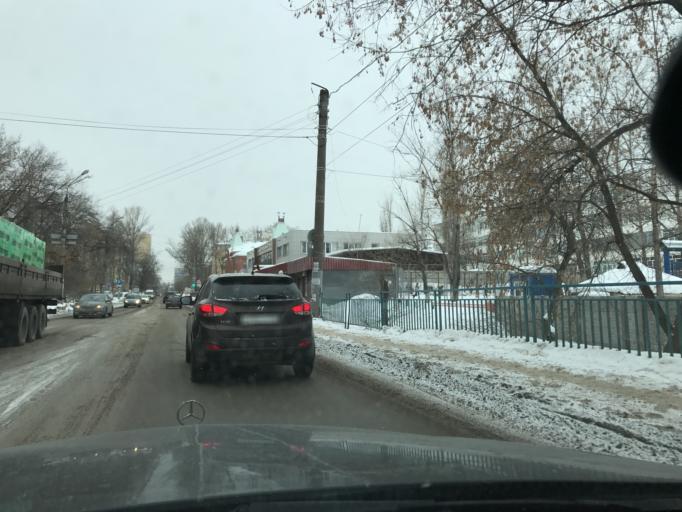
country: RU
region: Nizjnij Novgorod
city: Nizhniy Novgorod
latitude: 56.3322
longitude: 43.9614
